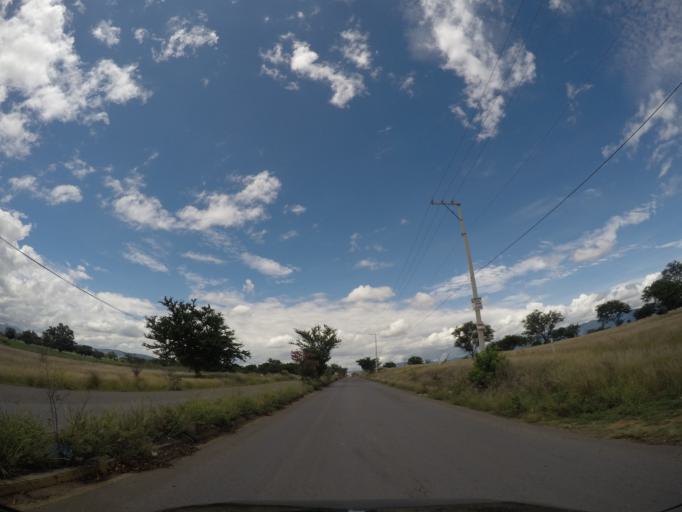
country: MX
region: Oaxaca
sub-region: Santa Cruz Xoxocotlan
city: San Isidro Monjas
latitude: 16.9895
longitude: -96.7451
